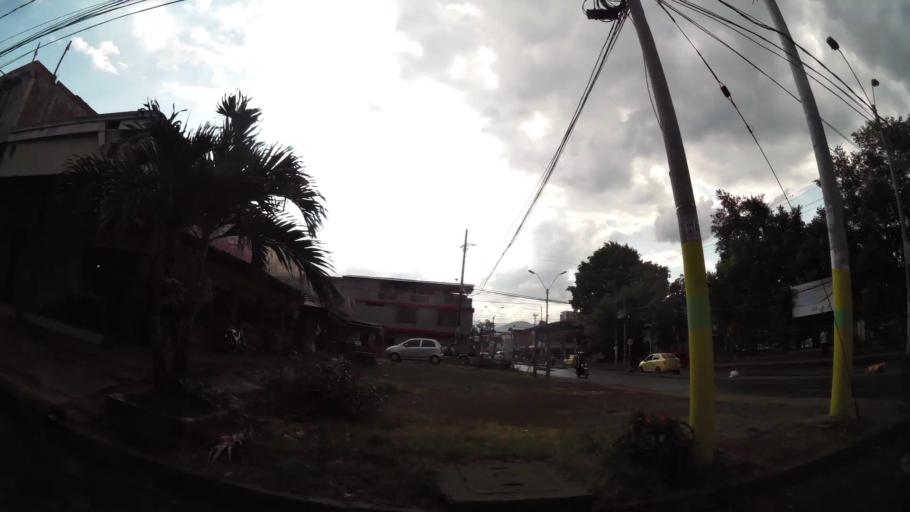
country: CO
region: Valle del Cauca
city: Cali
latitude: 3.4721
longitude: -76.4887
